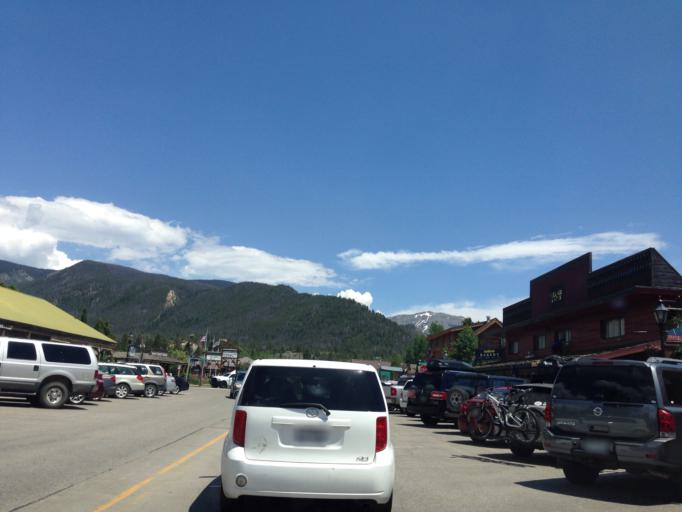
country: US
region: Colorado
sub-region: Grand County
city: Granby
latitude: 40.2518
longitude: -105.8204
